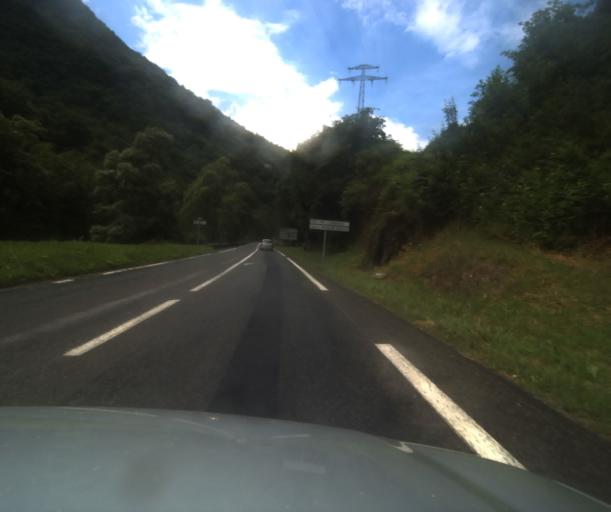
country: FR
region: Midi-Pyrenees
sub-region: Departement des Hautes-Pyrenees
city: Pierrefitte-Nestalas
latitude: 42.9500
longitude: -0.0645
